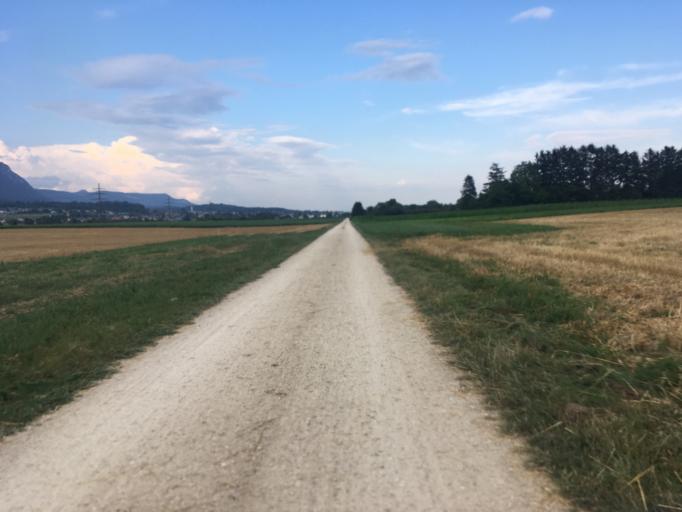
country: CH
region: Solothurn
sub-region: Bezirk Lebern
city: Selzach
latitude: 47.2023
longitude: 7.4731
